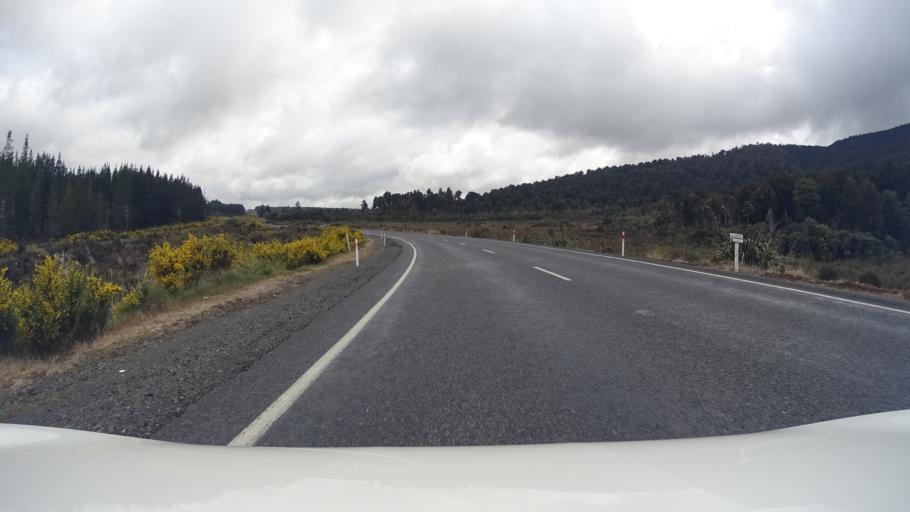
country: NZ
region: Manawatu-Wanganui
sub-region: Ruapehu District
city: Waiouru
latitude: -39.2217
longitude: 175.4001
